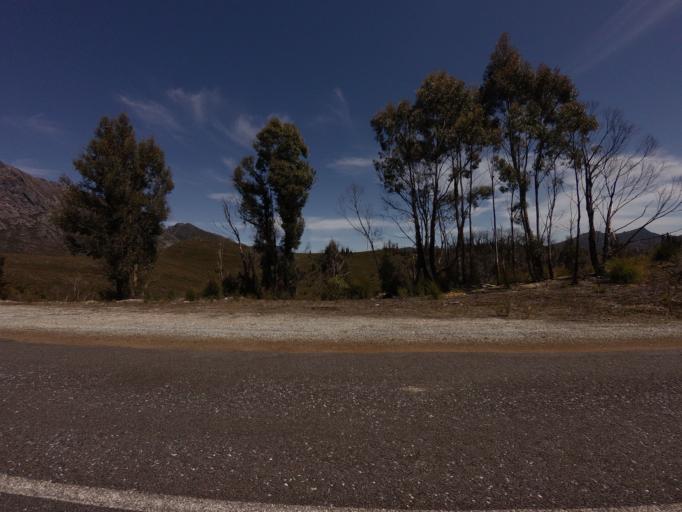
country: AU
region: Tasmania
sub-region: Huon Valley
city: Geeveston
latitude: -42.8520
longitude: 146.2355
